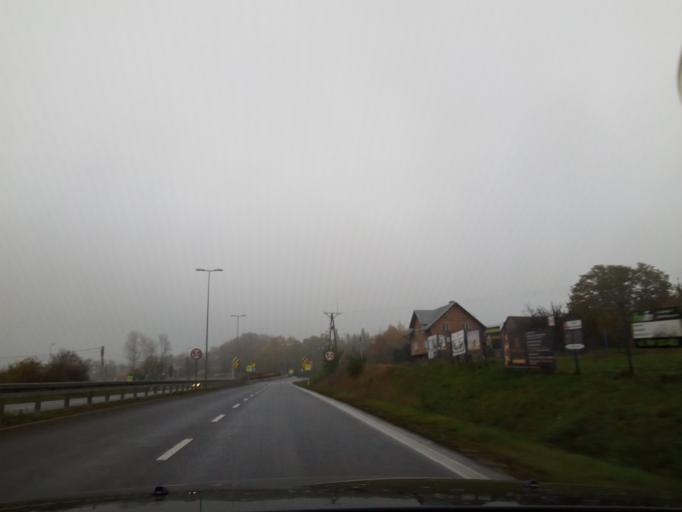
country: PL
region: Lesser Poland Voivodeship
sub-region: Powiat wielicki
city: Kokotow
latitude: 50.1133
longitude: 20.0862
